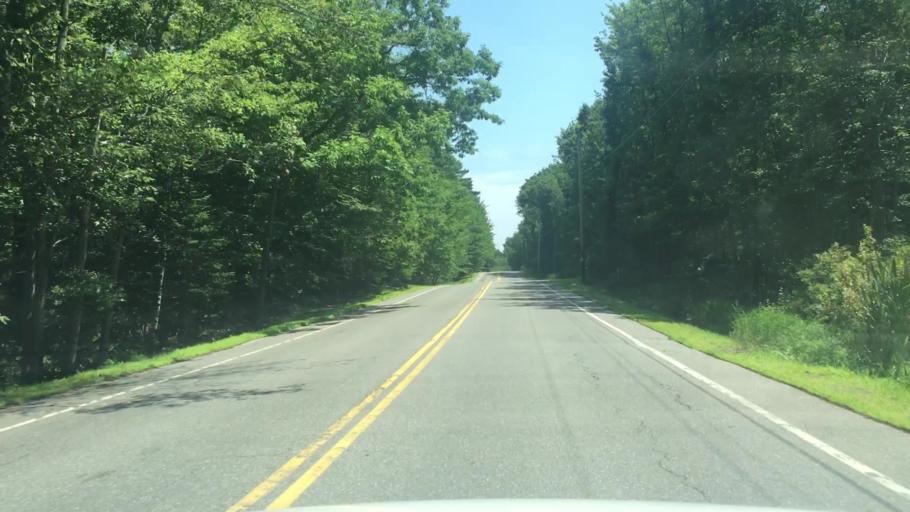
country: US
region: Maine
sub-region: Cumberland County
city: Falmouth
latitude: 43.7402
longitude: -70.2522
